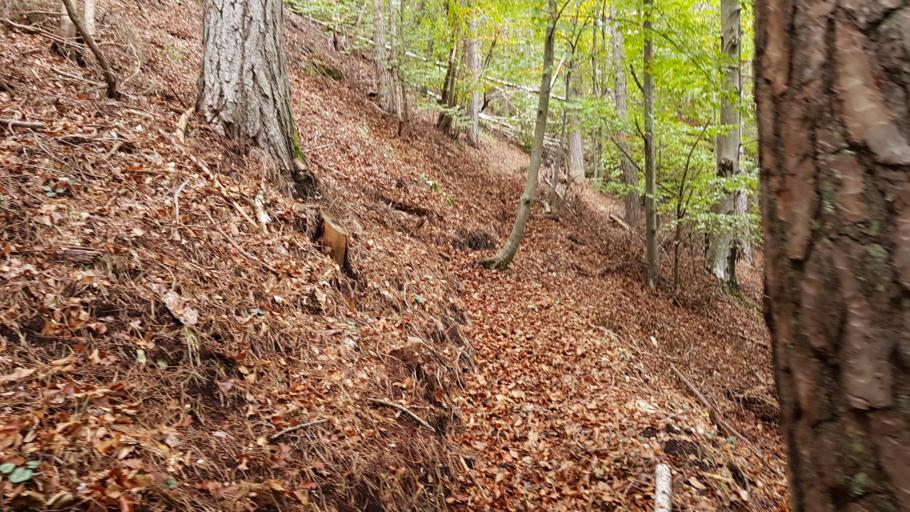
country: IT
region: Friuli Venezia Giulia
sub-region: Provincia di Udine
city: Chiusaforte
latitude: 46.4056
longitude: 13.3485
